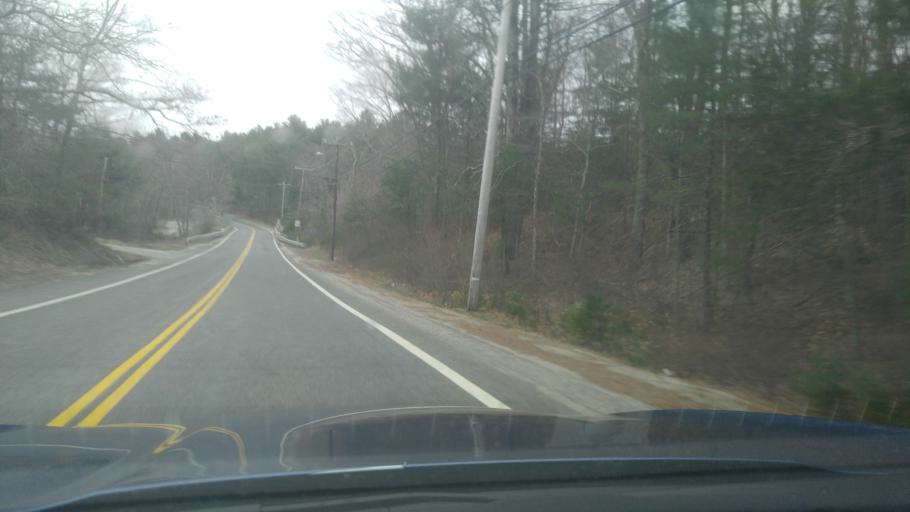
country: US
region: Rhode Island
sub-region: Kent County
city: West Greenwich
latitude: 41.6658
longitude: -71.6203
